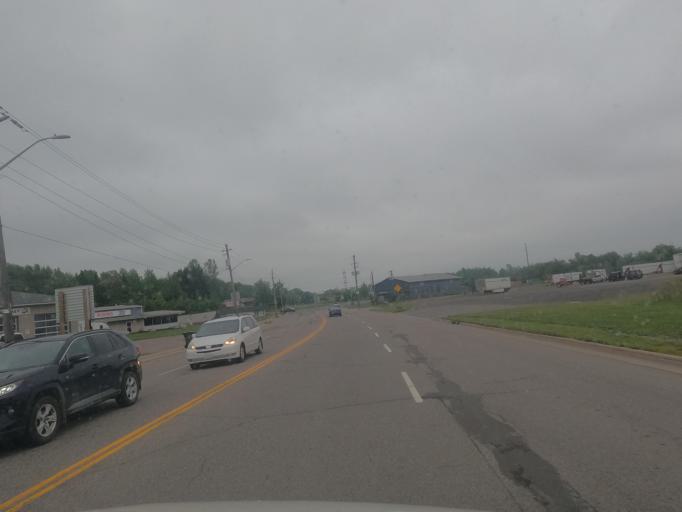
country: CA
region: Ontario
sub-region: Algoma
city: Sault Ste. Marie
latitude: 46.5379
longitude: -84.3455
